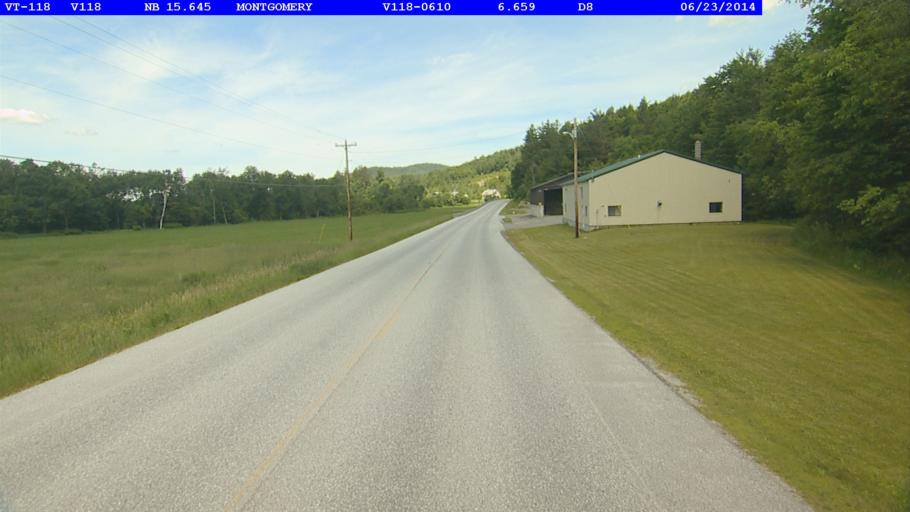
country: US
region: Vermont
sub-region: Franklin County
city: Richford
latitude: 44.8894
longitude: -72.6202
